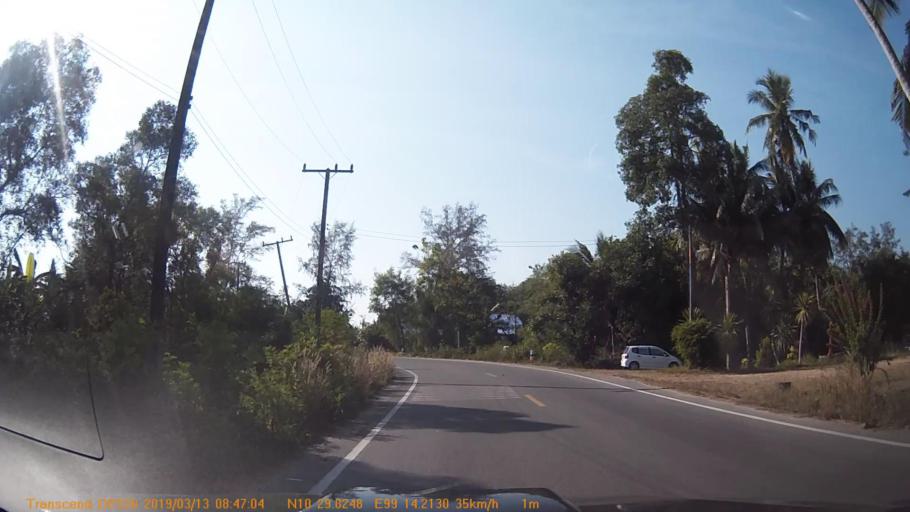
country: TH
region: Chumphon
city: Chumphon
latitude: 10.4969
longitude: 99.2370
